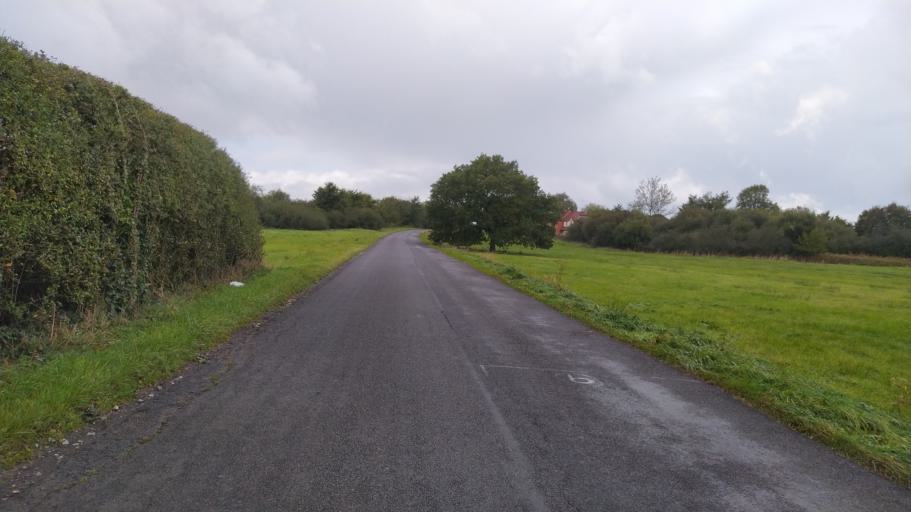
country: GB
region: England
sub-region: Dorset
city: Shaftesbury
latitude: 51.0448
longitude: -2.1775
